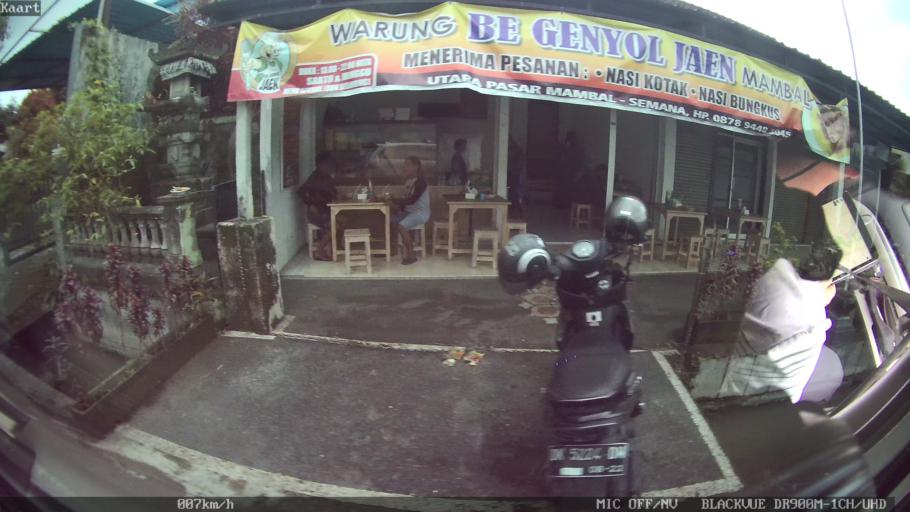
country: ID
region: Bali
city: Banjar Mambalkajanan
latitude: -8.5479
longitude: 115.2206
